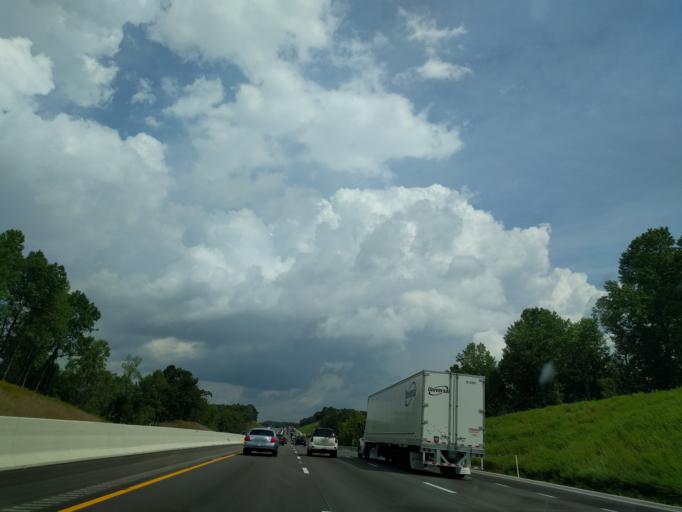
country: US
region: Kentucky
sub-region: Hart County
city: Munfordville
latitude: 37.3867
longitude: -85.8859
